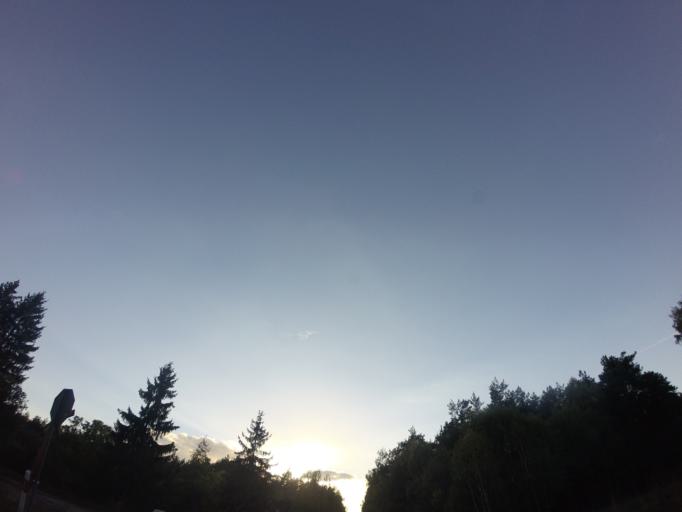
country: PL
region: Greater Poland Voivodeship
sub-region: Powiat miedzychodzki
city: Miedzychod
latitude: 52.5024
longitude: 15.9477
